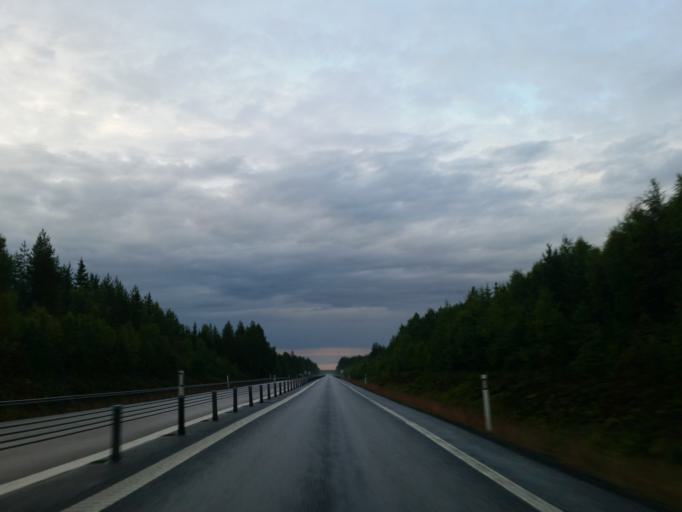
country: SE
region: Vaesterbotten
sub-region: Umea Kommun
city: Saevar
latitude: 63.9698
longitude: 20.7098
